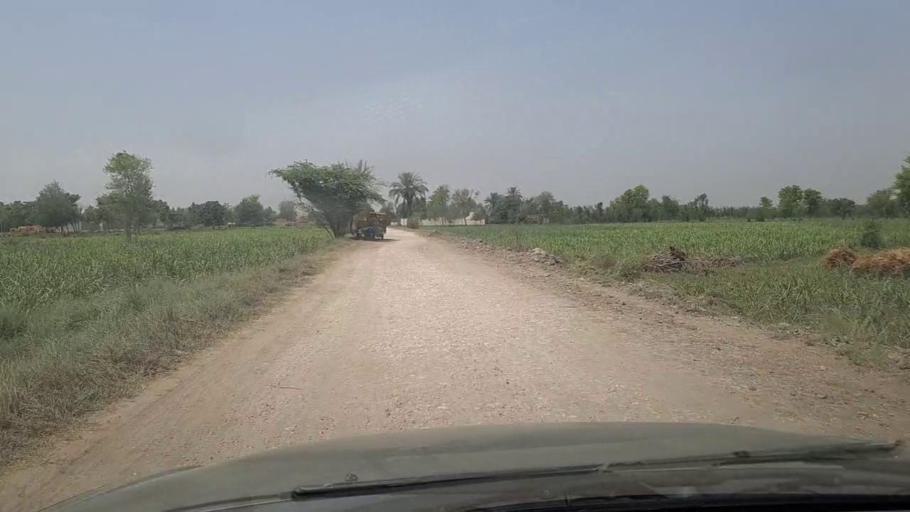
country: PK
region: Sindh
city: Adilpur
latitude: 27.9342
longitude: 69.2710
